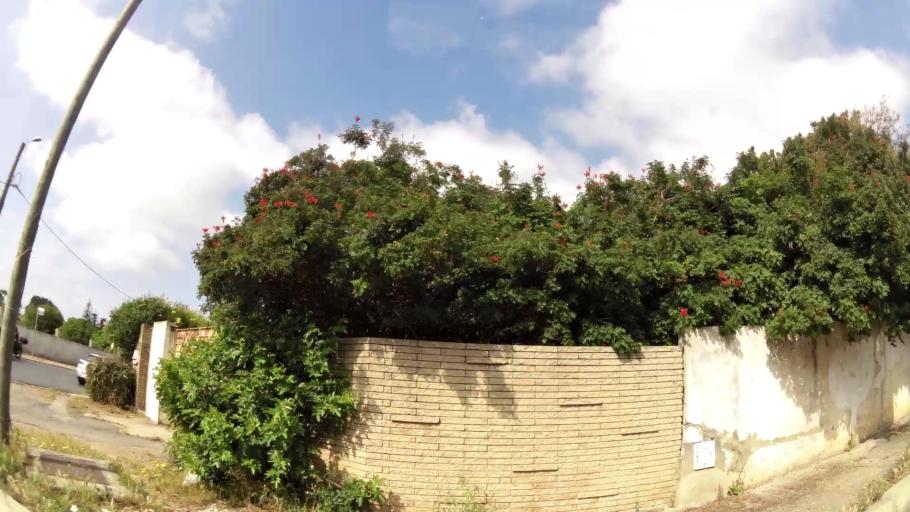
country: MA
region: Rabat-Sale-Zemmour-Zaer
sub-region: Rabat
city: Rabat
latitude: 33.9720
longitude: -6.8525
